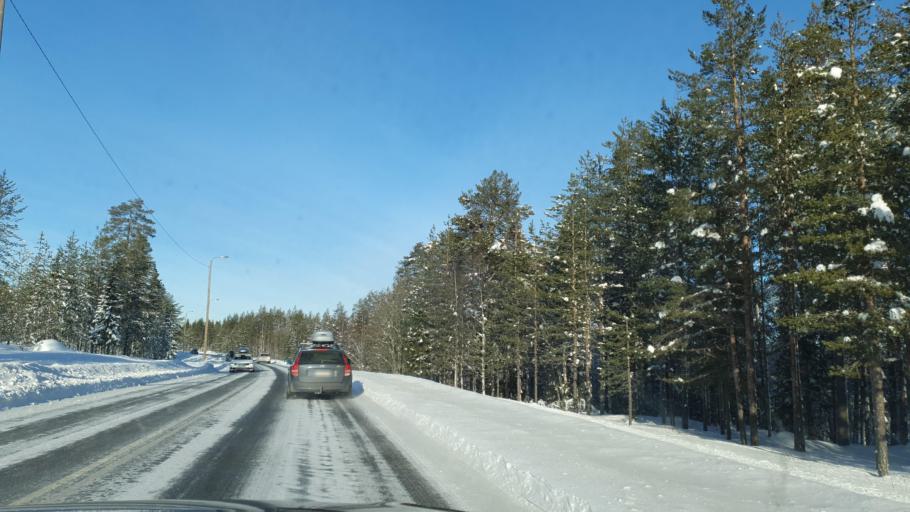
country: FI
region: Lapland
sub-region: Torniolaakso
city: Ylitornio
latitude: 66.2109
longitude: 23.7976
